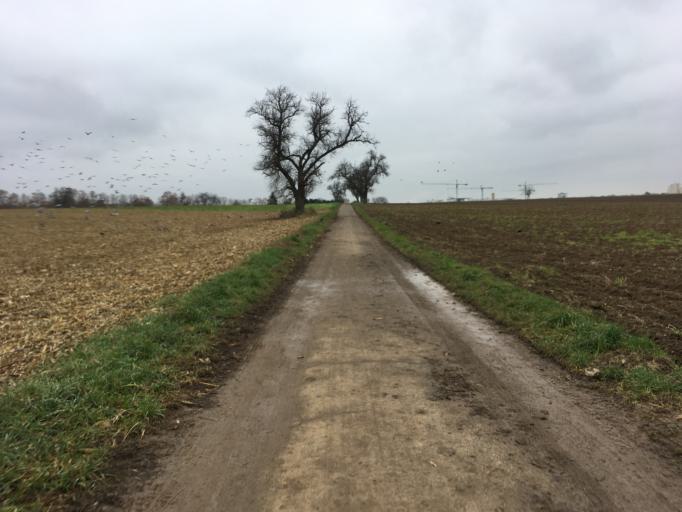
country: DE
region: Baden-Wuerttemberg
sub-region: Regierungsbezirk Stuttgart
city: Heilbronn
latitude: 49.1632
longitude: 9.1932
